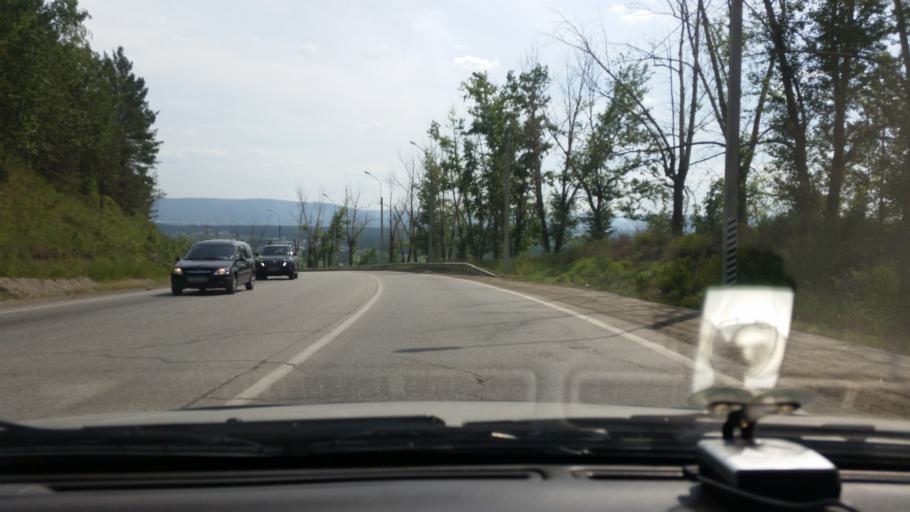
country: RU
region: Irkutsk
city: Smolenshchina
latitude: 52.2264
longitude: 104.1386
